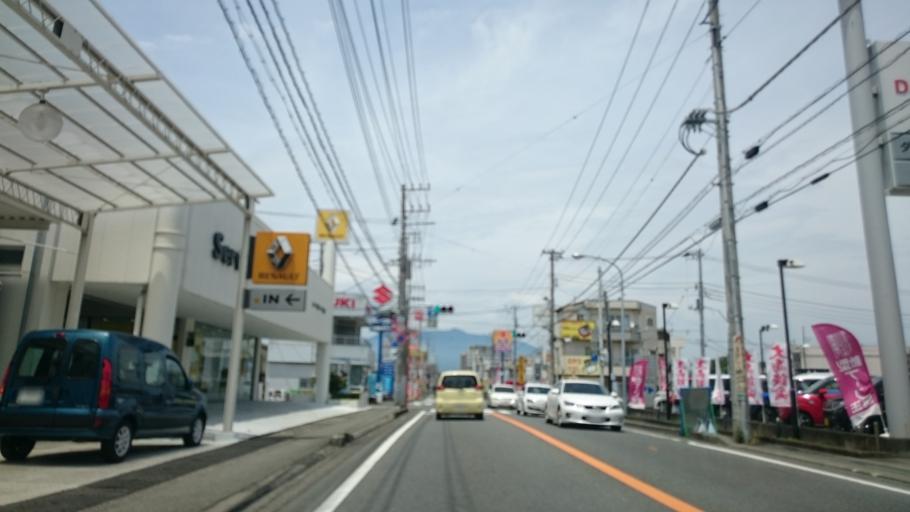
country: JP
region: Shizuoka
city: Numazu
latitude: 35.0840
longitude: 138.8690
